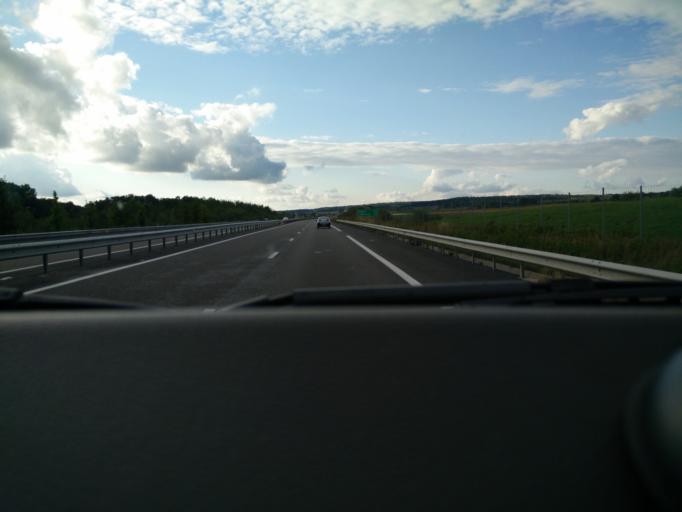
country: FR
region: Lorraine
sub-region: Departement de Meurthe-et-Moselle
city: Baccarat
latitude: 48.4769
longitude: 6.7189
